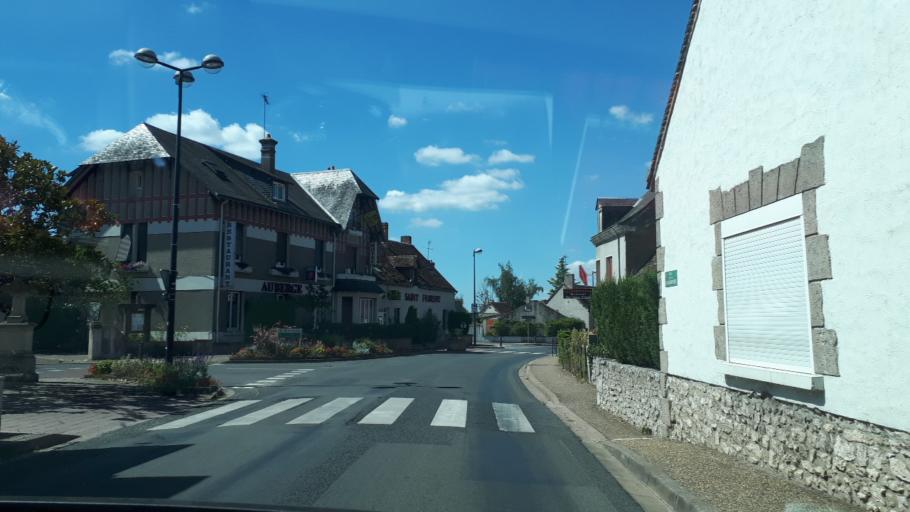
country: FR
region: Centre
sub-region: Departement du Loir-et-Cher
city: Mont-pres-Chambord
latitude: 47.5628
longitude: 1.4629
